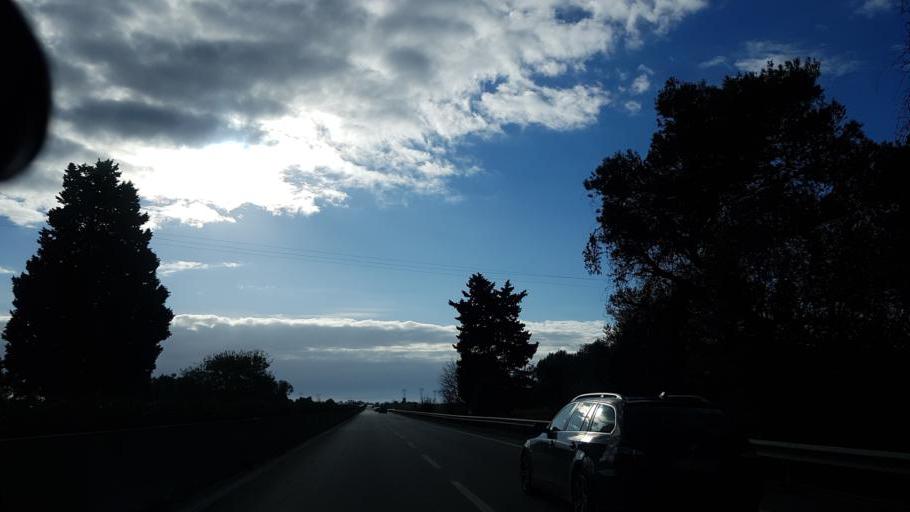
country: IT
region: Apulia
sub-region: Provincia di Brindisi
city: La Rosa
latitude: 40.5754
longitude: 17.9812
